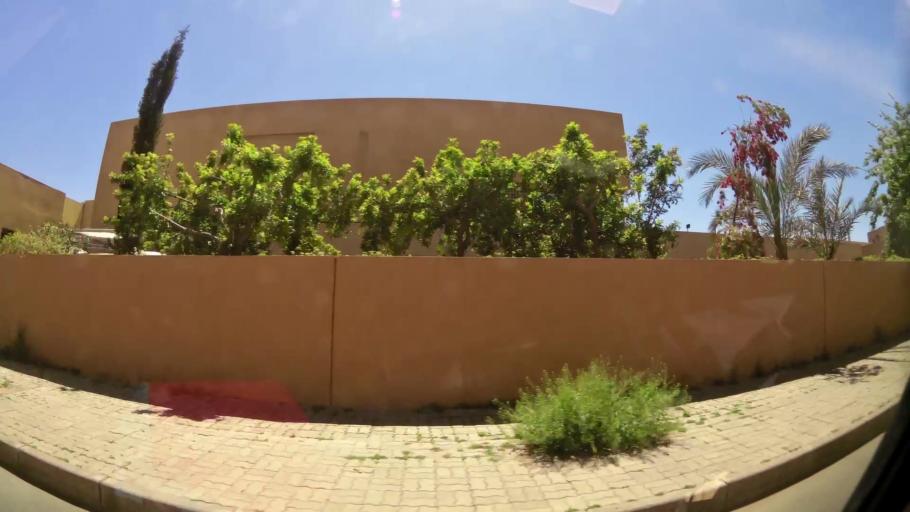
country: MA
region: Marrakech-Tensift-Al Haouz
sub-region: Marrakech
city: Marrakesh
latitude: 31.6458
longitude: -7.9978
